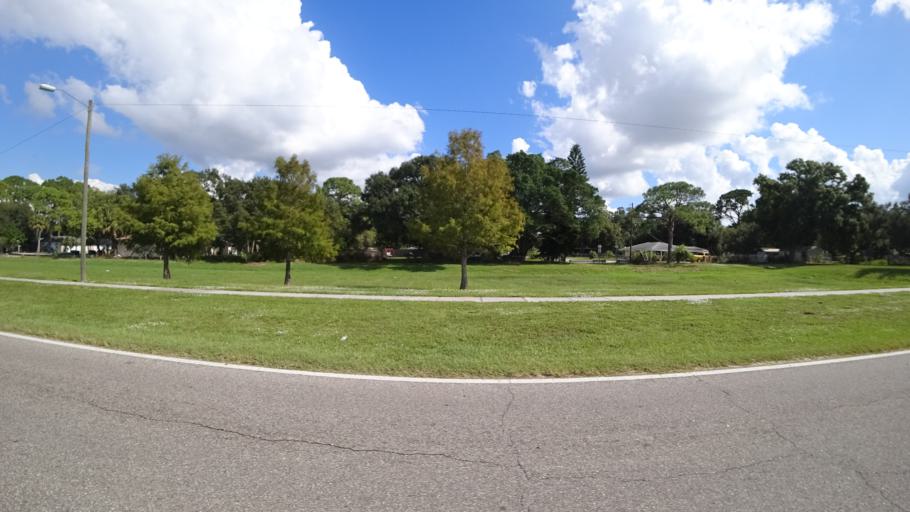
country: US
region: Florida
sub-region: Manatee County
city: Whitfield
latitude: 27.4356
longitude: -82.5554
